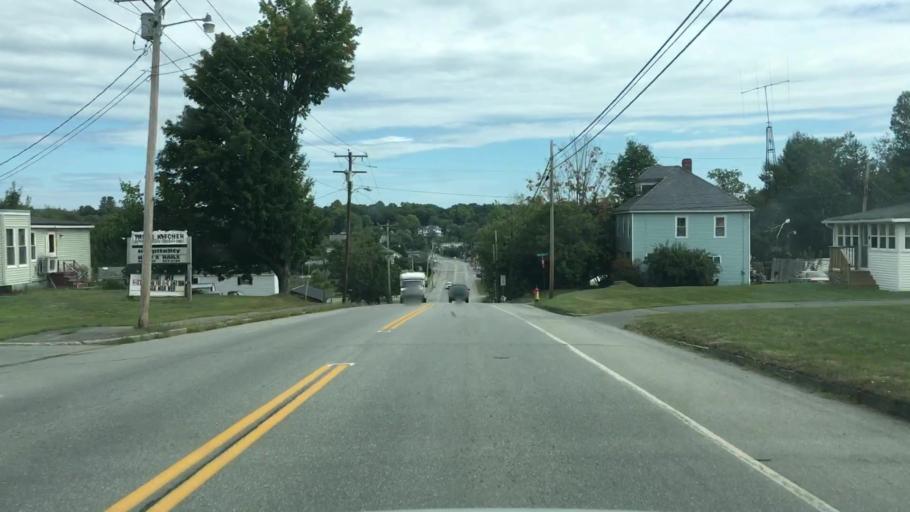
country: US
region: Maine
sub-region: Piscataquis County
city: Milo
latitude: 45.2492
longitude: -68.9944
